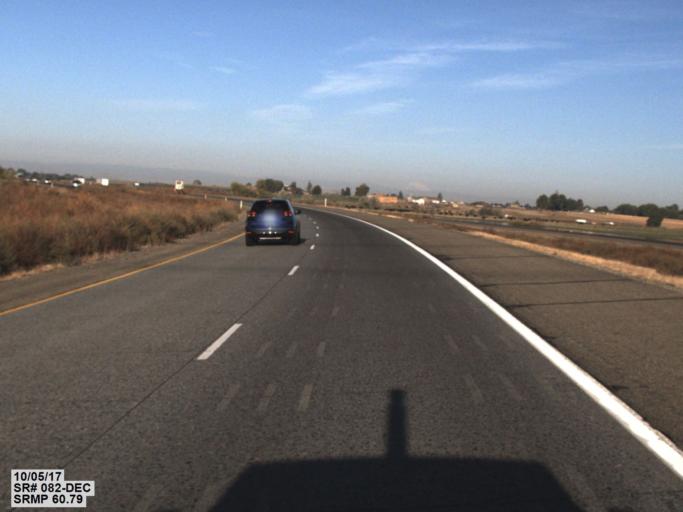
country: US
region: Washington
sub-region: Yakima County
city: Granger
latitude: 46.3381
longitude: -120.1337
